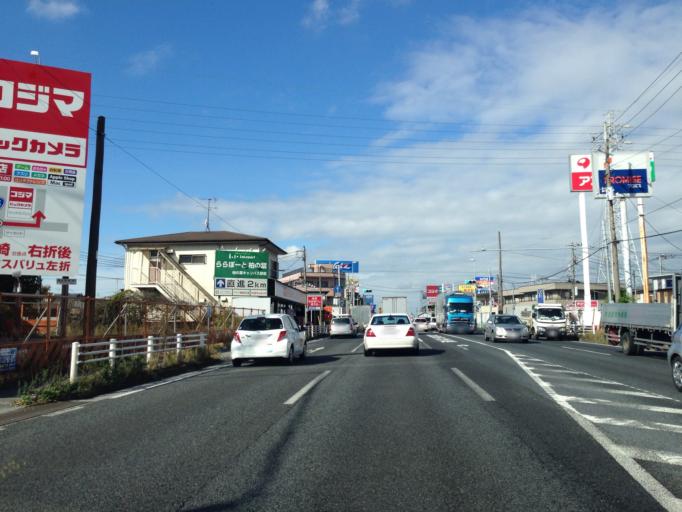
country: JP
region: Chiba
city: Kashiwa
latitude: 35.8767
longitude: 139.9683
